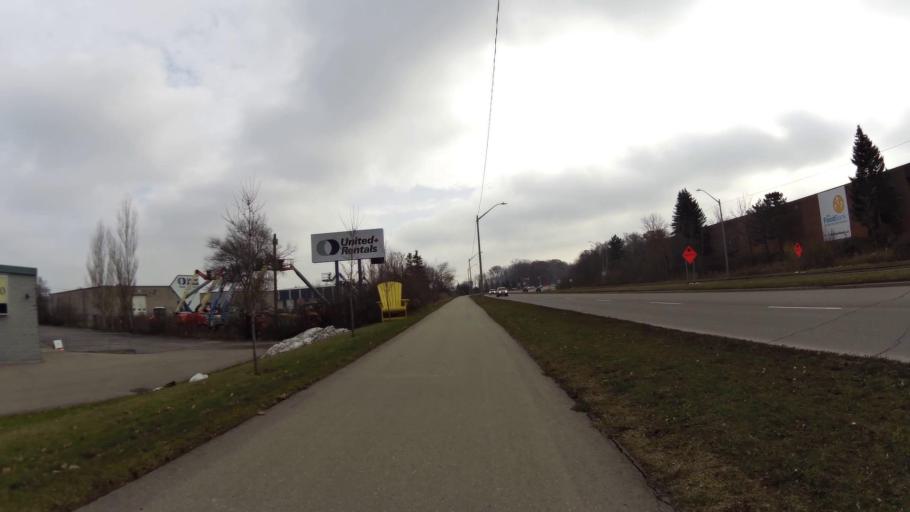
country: CA
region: Ontario
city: Kitchener
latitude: 43.4251
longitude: -80.4785
